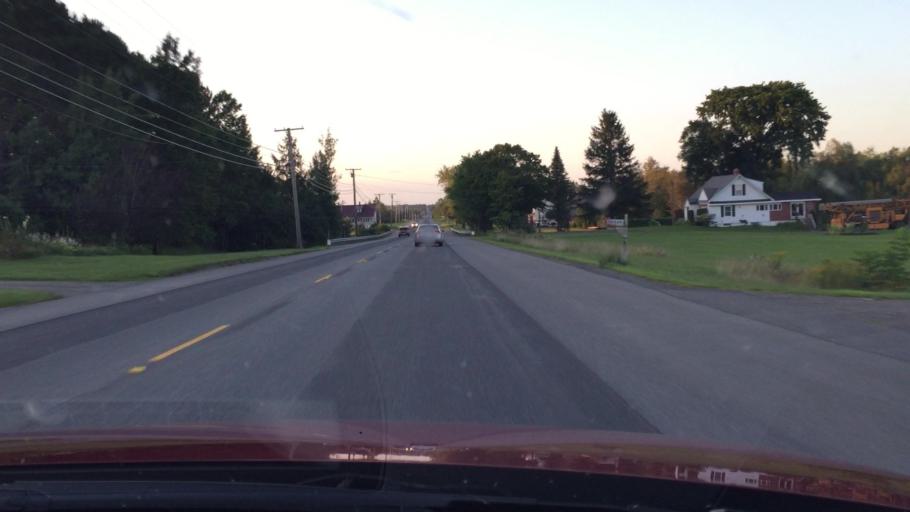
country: US
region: Maine
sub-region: Aroostook County
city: Houlton
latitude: 46.2323
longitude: -67.8409
